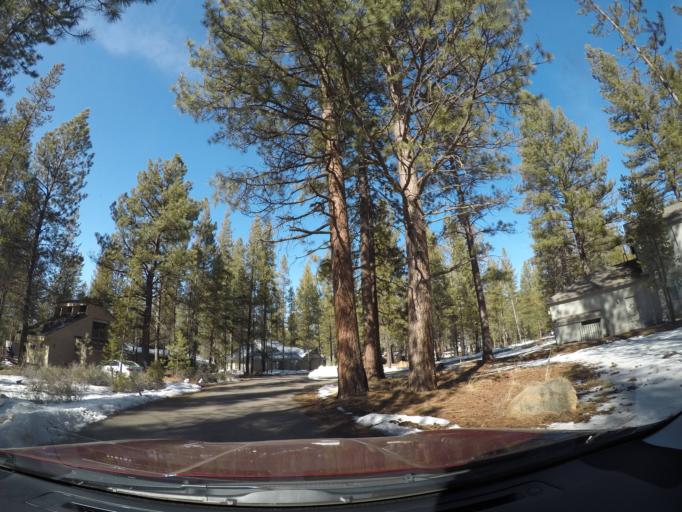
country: US
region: Oregon
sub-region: Deschutes County
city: Sunriver
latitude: 43.8717
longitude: -121.4326
